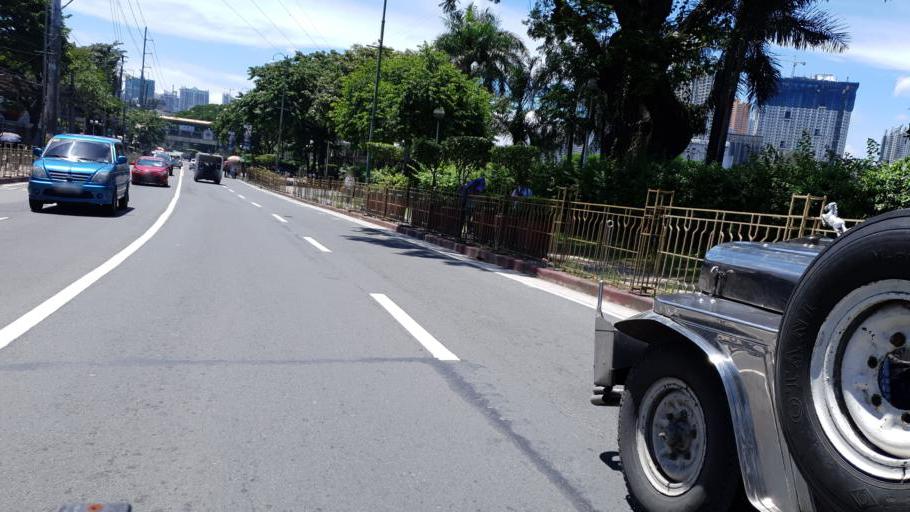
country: PH
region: Metro Manila
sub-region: Pasig
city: Pasig City
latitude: 14.5642
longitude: 121.0573
